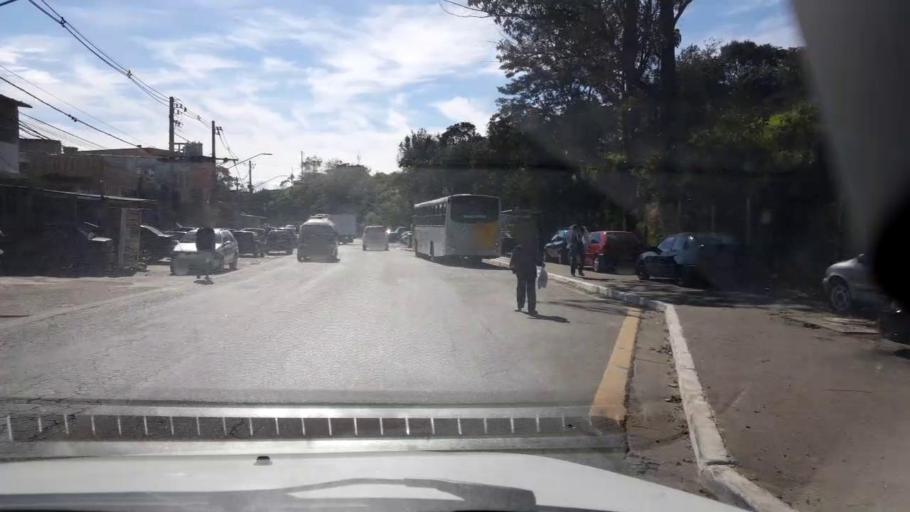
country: BR
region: Sao Paulo
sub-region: Ferraz De Vasconcelos
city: Ferraz de Vasconcelos
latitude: -23.5806
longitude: -46.4153
